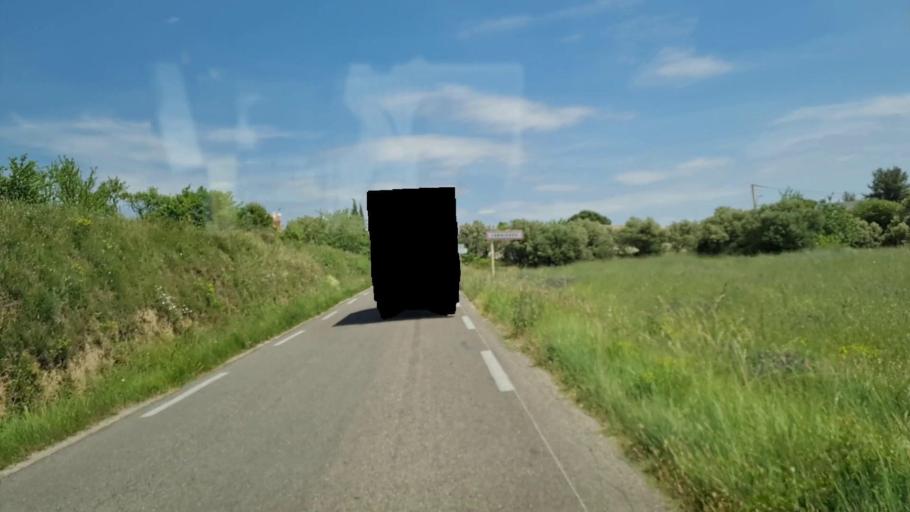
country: FR
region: Languedoc-Roussillon
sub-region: Departement du Gard
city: Cabrieres
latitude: 43.8976
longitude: 4.4728
